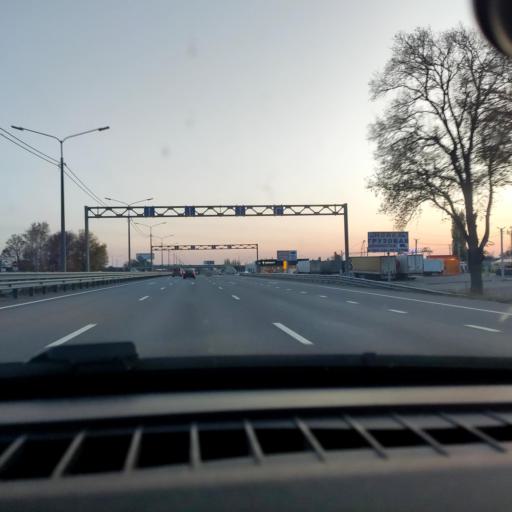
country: RU
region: Voronezj
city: Podgornoye
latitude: 51.8030
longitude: 39.2033
